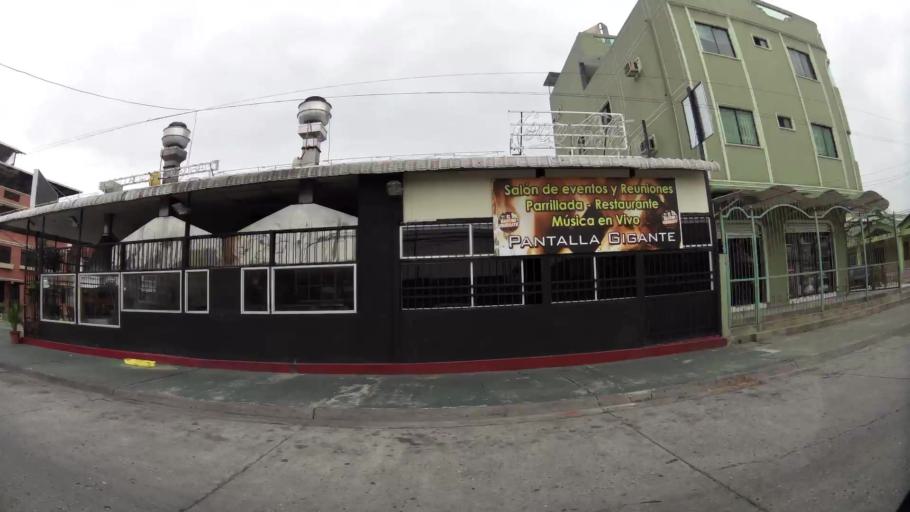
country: EC
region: Guayas
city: Eloy Alfaro
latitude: -2.1437
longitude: -79.8913
